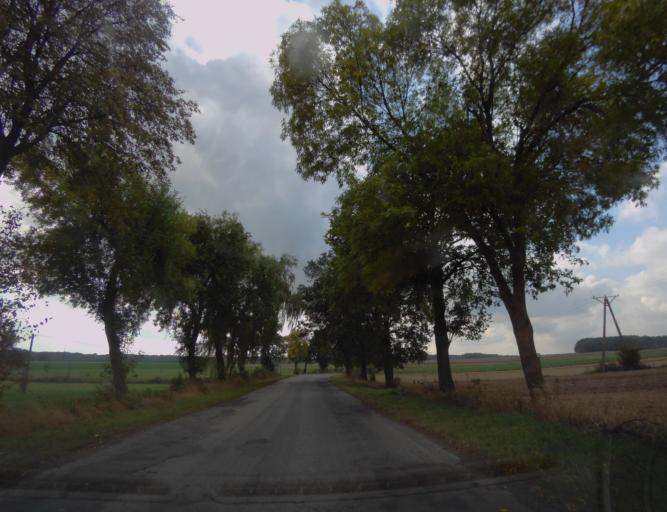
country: PL
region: Lublin Voivodeship
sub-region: Powiat krasnostawski
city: Zolkiewka
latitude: 50.8934
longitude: 22.8204
